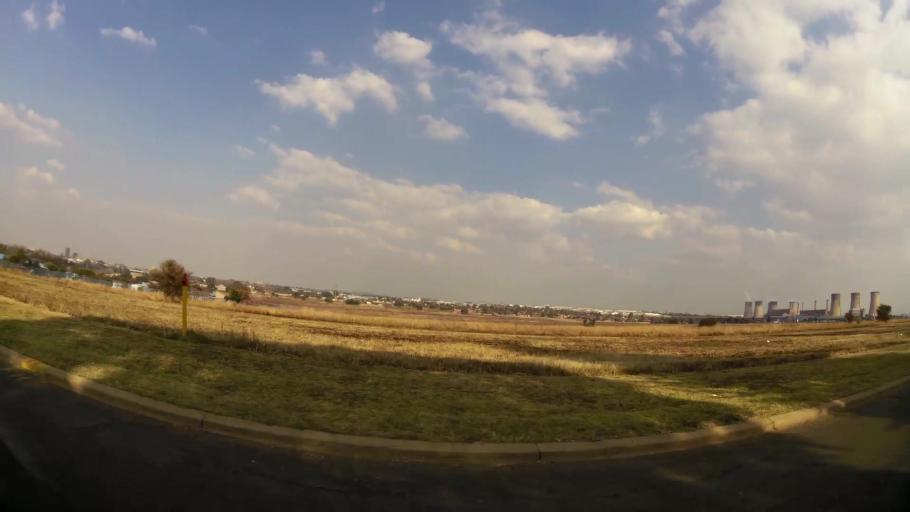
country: ZA
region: Gauteng
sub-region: City of Johannesburg Metropolitan Municipality
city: Modderfontein
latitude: -26.1002
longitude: 28.1999
